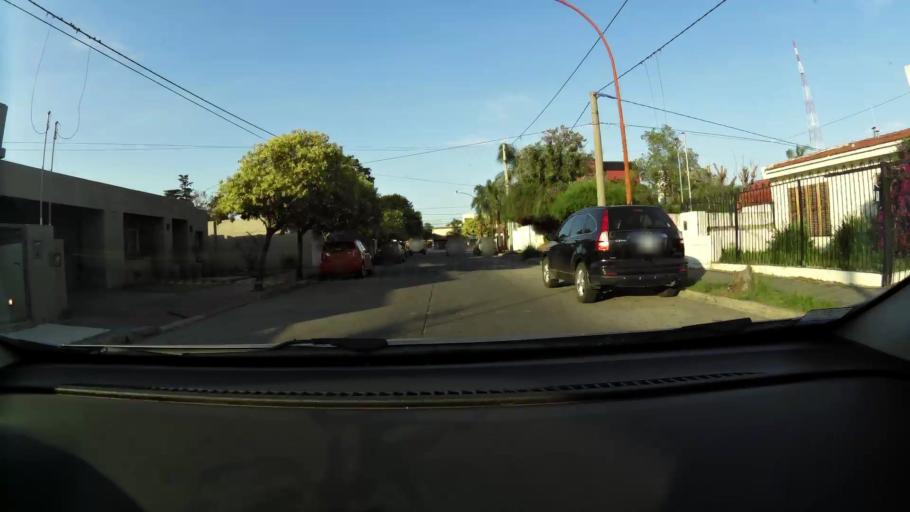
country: AR
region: Cordoba
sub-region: Departamento de Capital
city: Cordoba
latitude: -31.3814
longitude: -64.2301
